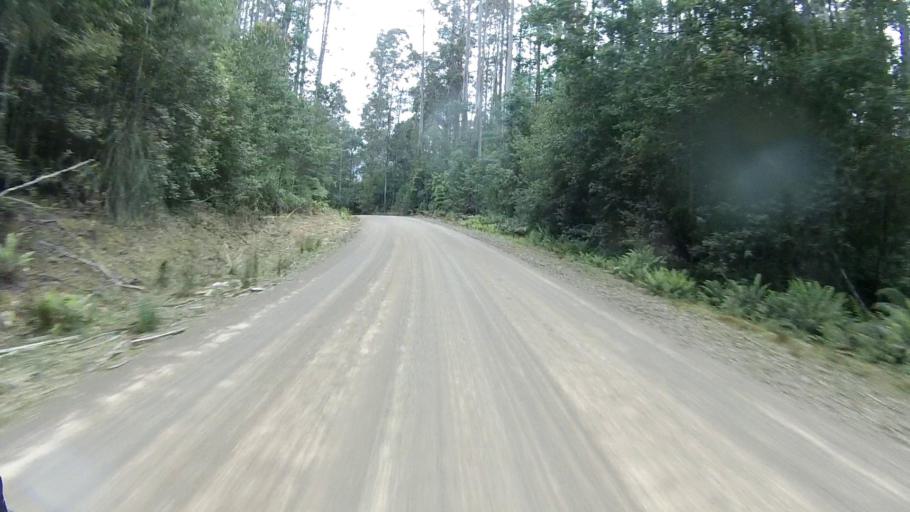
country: AU
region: Tasmania
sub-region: Sorell
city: Sorell
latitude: -42.7095
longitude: 147.8401
